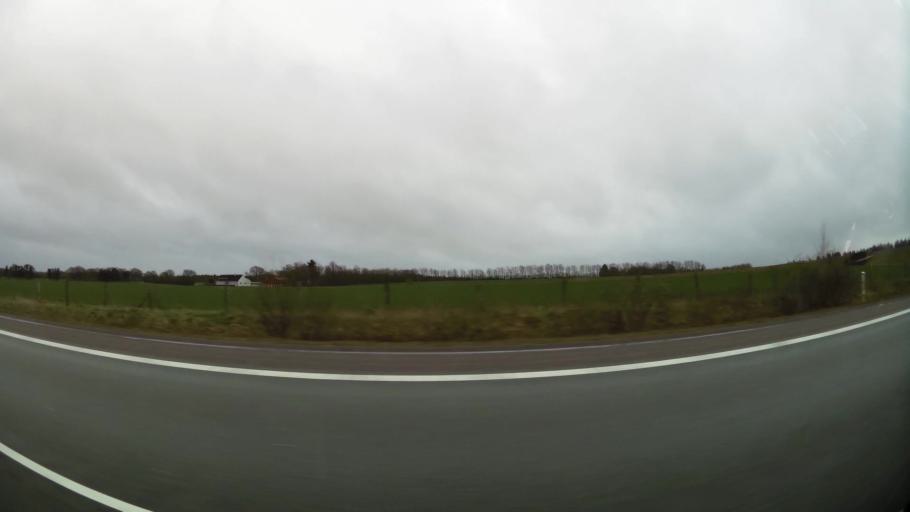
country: DK
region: Central Jutland
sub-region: Herning Kommune
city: Snejbjerg
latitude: 56.1879
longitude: 8.9190
